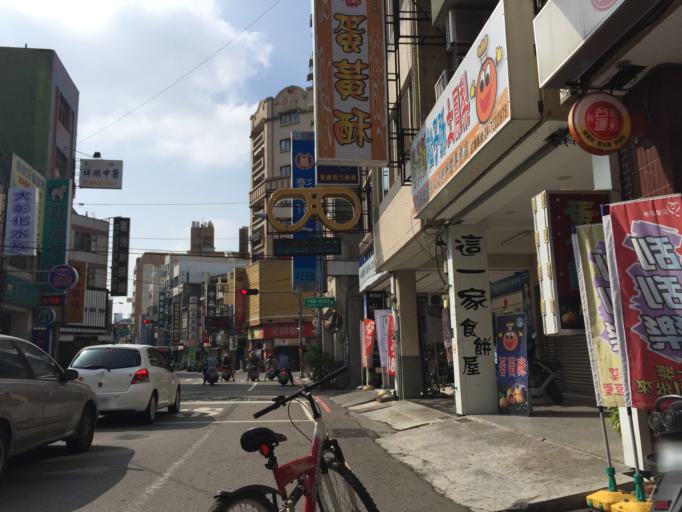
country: TW
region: Taiwan
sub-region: Changhua
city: Chang-hua
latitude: 24.0838
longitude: 120.5477
